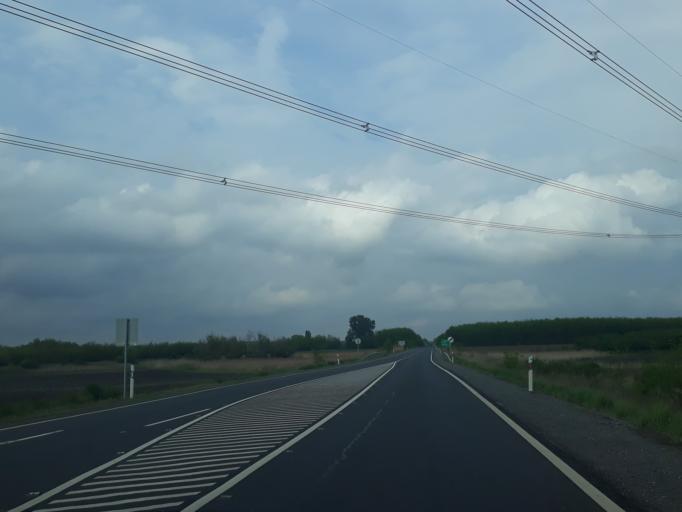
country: HU
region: Szabolcs-Szatmar-Bereg
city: Nyirtass
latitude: 48.1265
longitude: 22.0104
